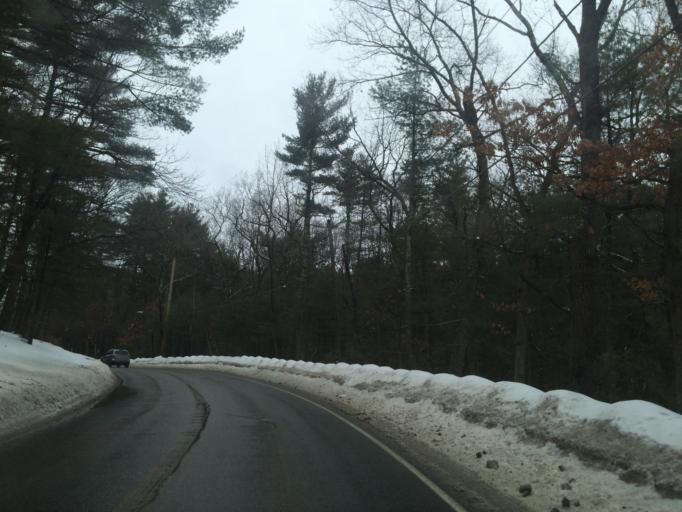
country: US
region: Massachusetts
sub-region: Middlesex County
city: Concord
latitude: 42.4336
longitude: -71.3358
